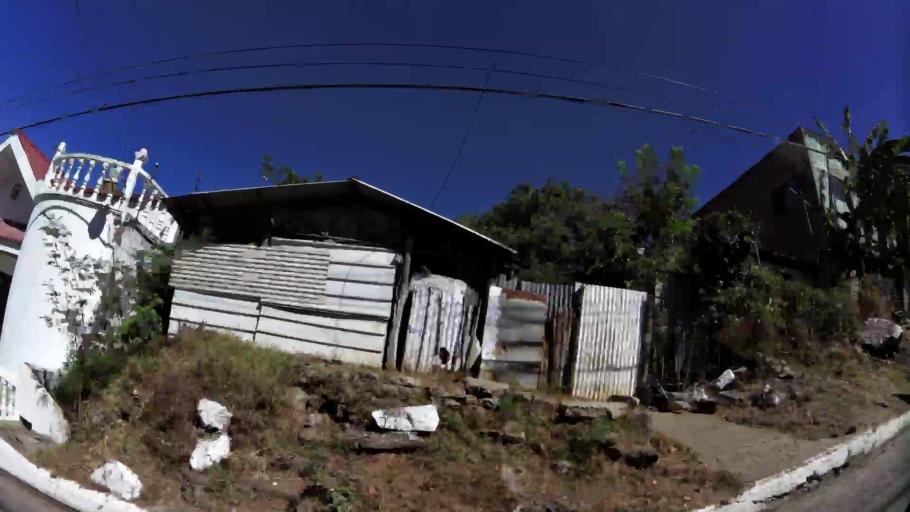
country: SV
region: La Libertad
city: San Juan Opico
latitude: 13.8753
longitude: -89.3542
